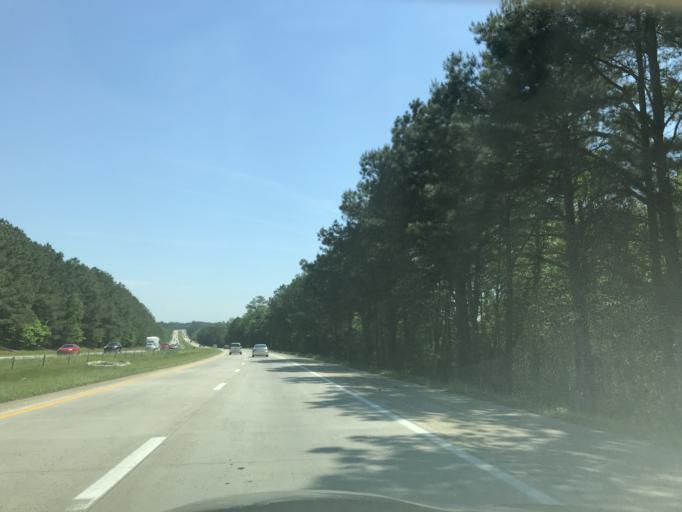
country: US
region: North Carolina
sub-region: Johnston County
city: Benson
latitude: 35.4680
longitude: -78.5476
